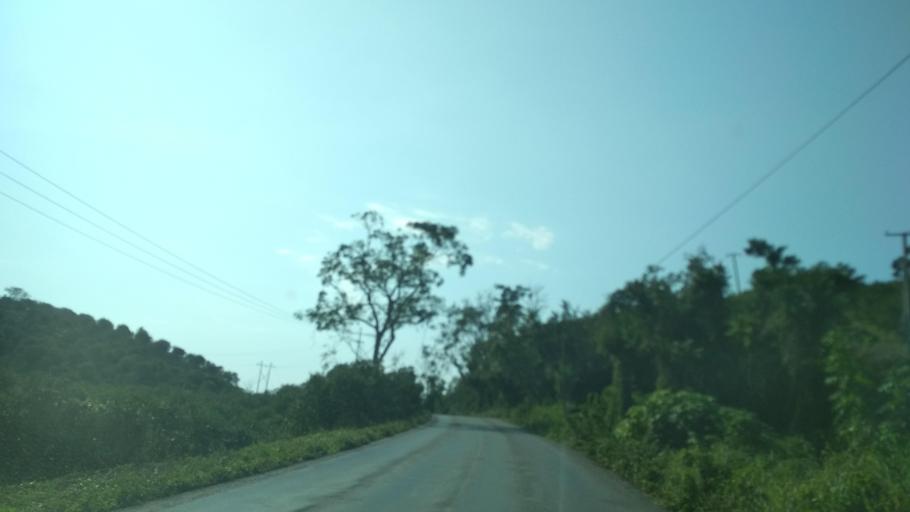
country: MX
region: Veracruz
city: Agua Dulce
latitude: 20.4019
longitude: -97.2231
